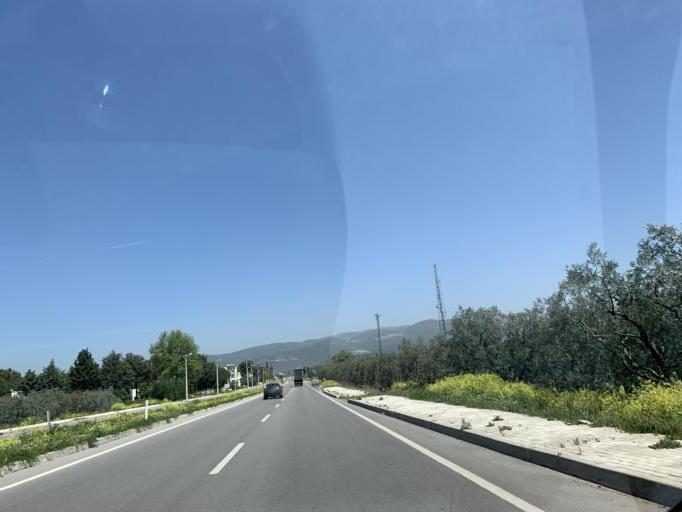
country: TR
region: Bursa
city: Iznik
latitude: 40.4044
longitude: 29.7012
